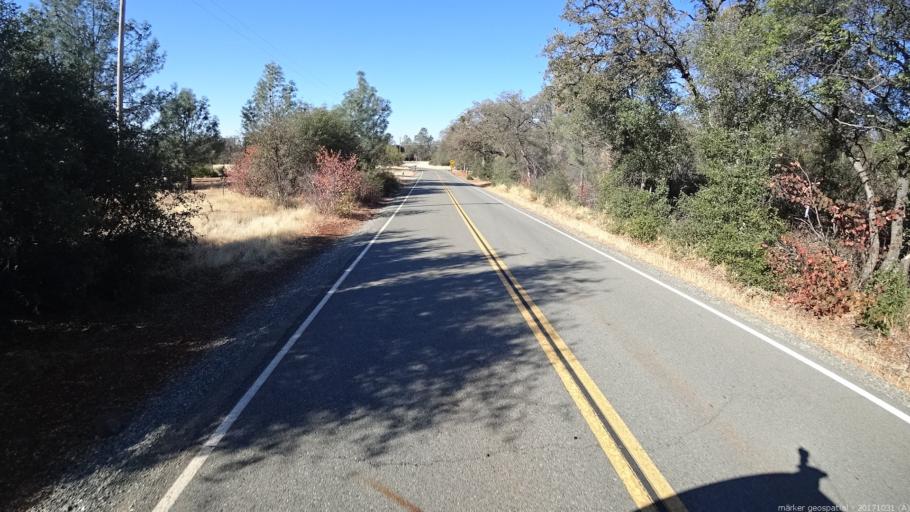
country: US
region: California
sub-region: Shasta County
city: Shingletown
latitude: 40.4463
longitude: -121.8970
